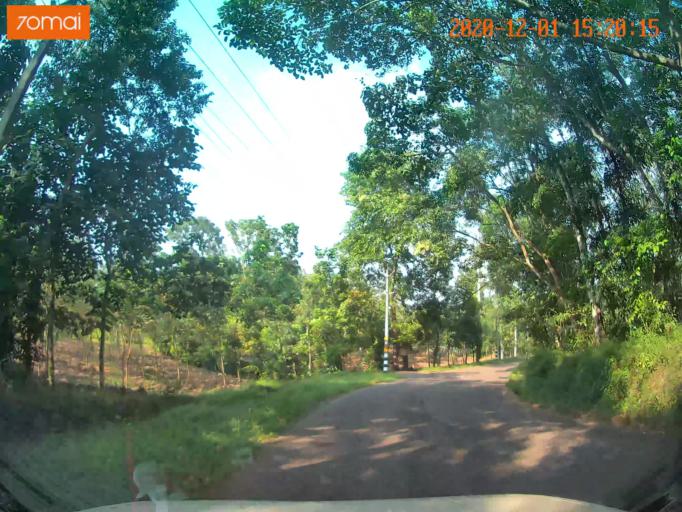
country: IN
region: Kerala
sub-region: Ernakulam
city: Ramamangalam
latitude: 9.9419
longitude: 76.5381
